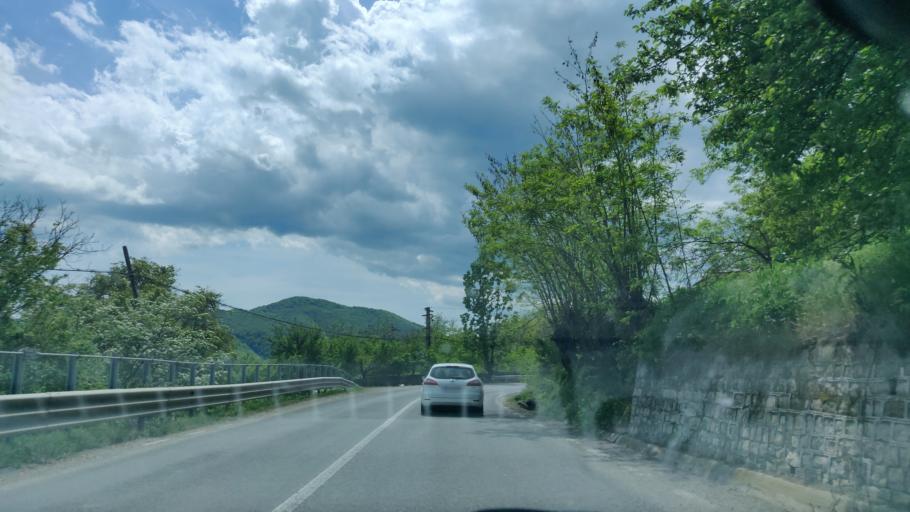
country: RO
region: Vrancea
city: Matacina
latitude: 45.8853
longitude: 26.8102
